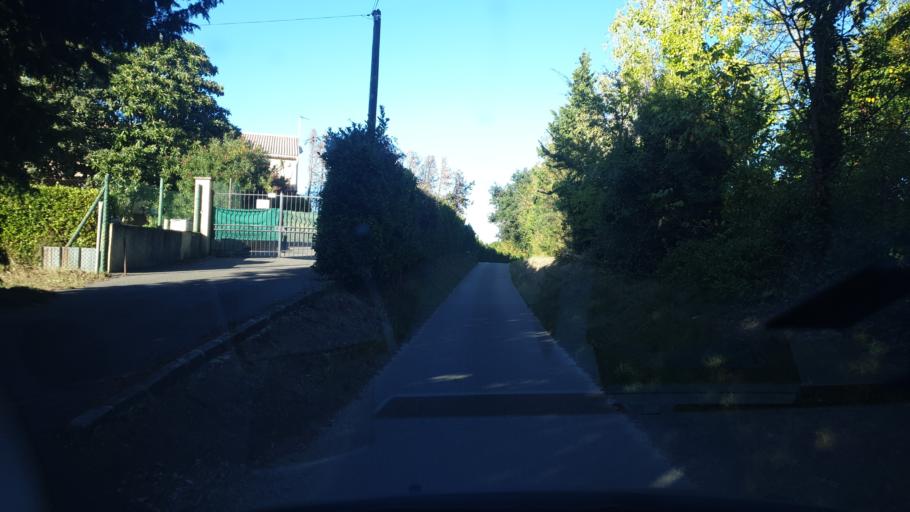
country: FR
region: Provence-Alpes-Cote d'Azur
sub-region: Departement du Vaucluse
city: Loriol-du-Comtat
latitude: 44.0578
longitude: 5.0059
